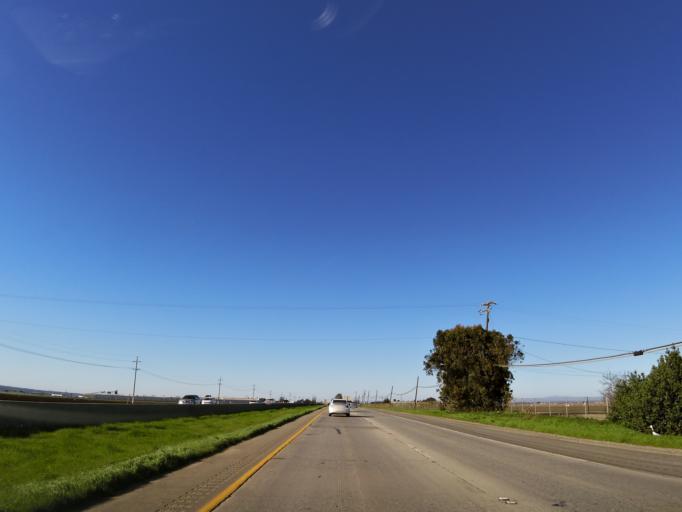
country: US
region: California
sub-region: Monterey County
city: Chualar
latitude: 36.6195
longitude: -121.5760
